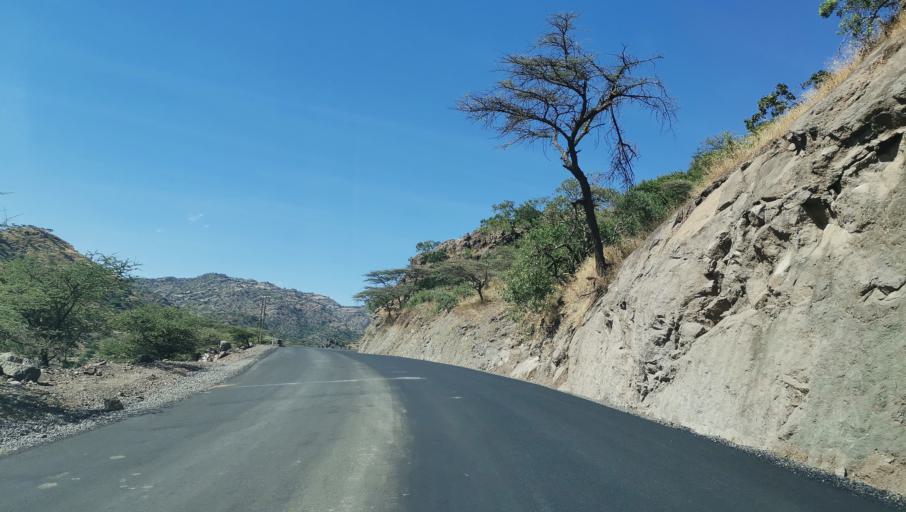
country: ET
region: Amhara
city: Lalibela
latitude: 12.2366
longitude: 39.0263
